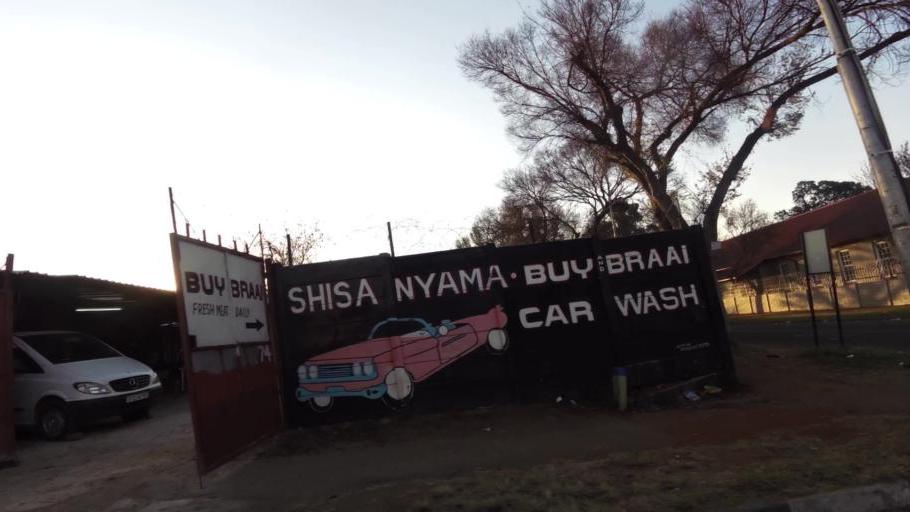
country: ZA
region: Gauteng
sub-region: City of Johannesburg Metropolitan Municipality
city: Johannesburg
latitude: -26.1731
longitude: 27.9637
